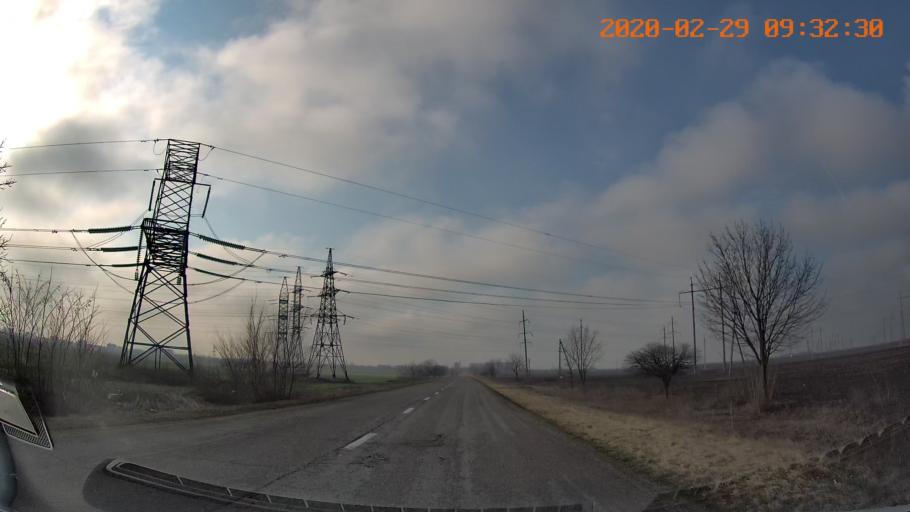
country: MD
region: Telenesti
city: Dnestrovsc
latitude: 46.6387
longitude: 29.9057
